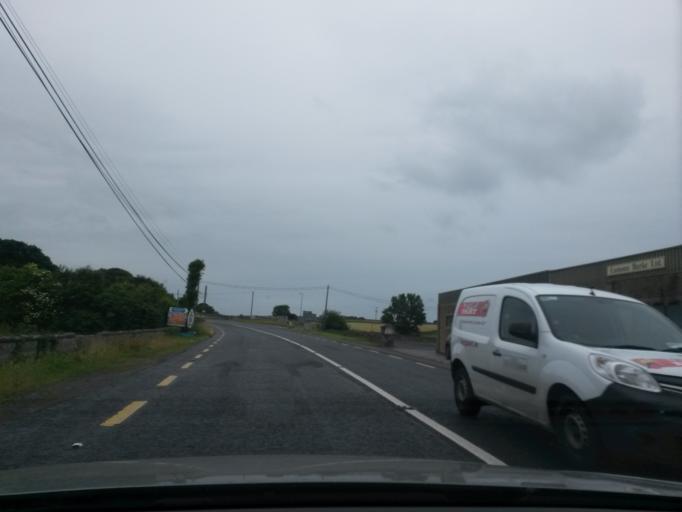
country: IE
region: Connaught
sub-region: Sligo
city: Strandhill
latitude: 54.2455
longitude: -8.7134
